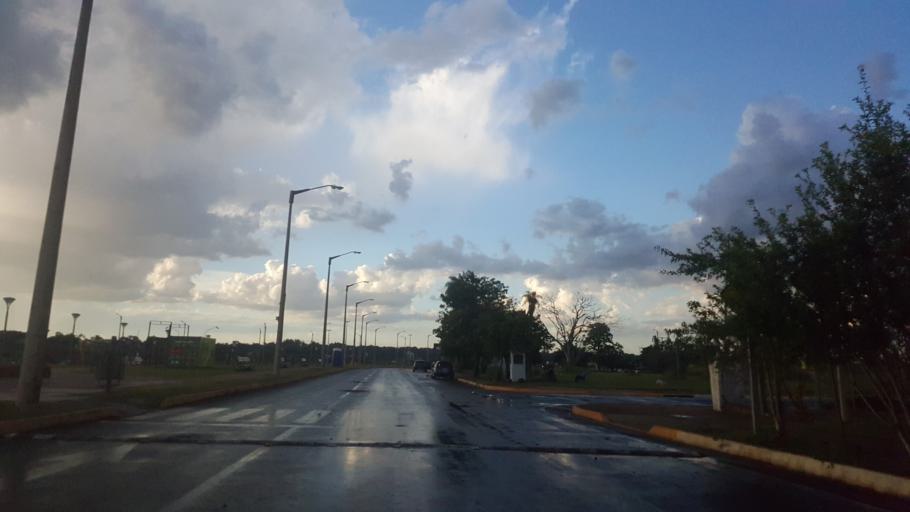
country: PY
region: Itapua
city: Encarnacion
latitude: -27.3249
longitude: -55.8758
